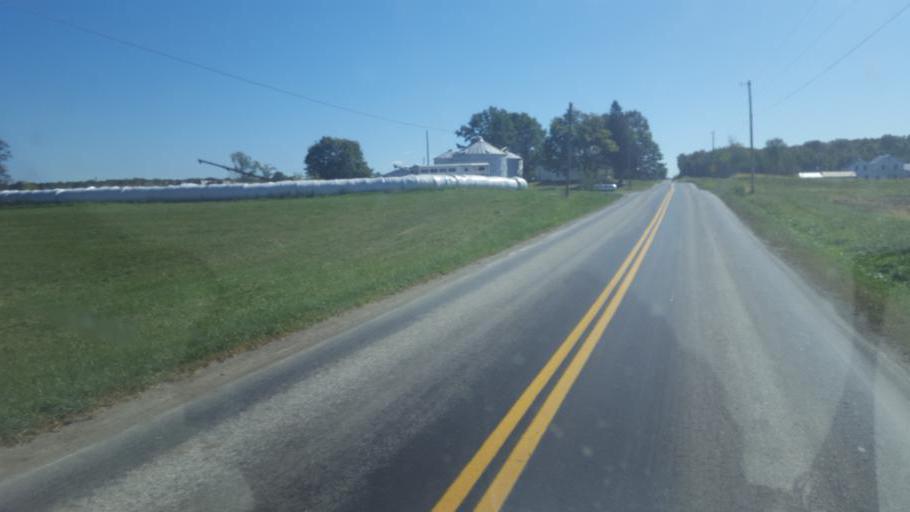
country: US
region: Ohio
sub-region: Wayne County
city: West Salem
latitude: 40.9734
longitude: -82.1629
